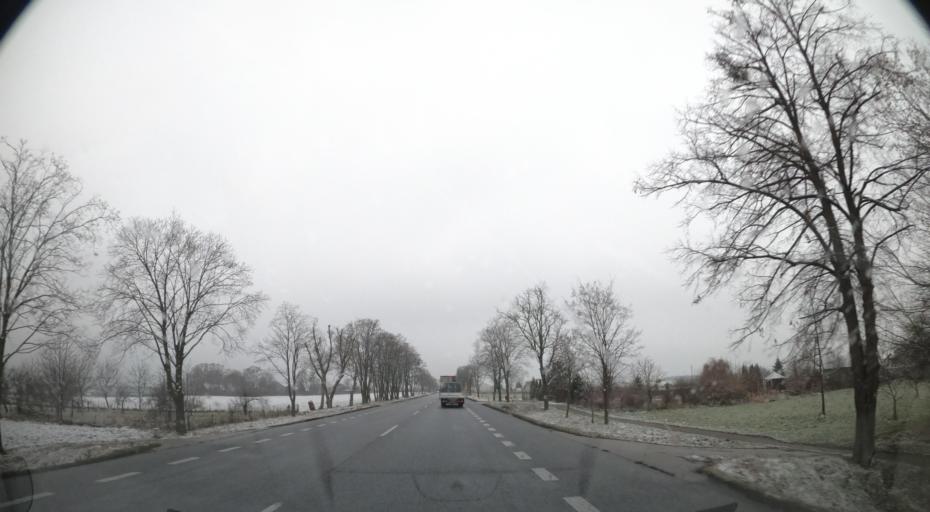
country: PL
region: Masovian Voivodeship
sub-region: Powiat sochaczewski
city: Teresin
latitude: 52.2154
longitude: 20.3920
